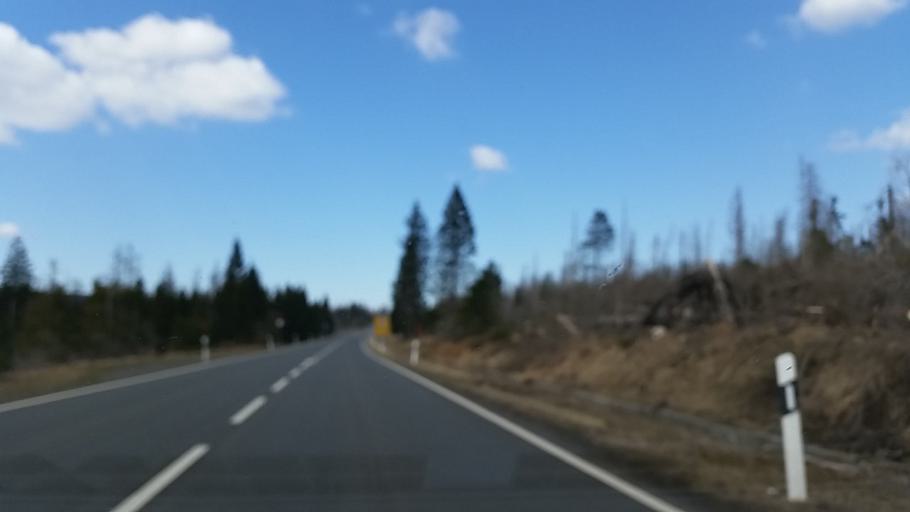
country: DE
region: Lower Saxony
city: Sankt Andreasberg
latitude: 51.7584
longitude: 10.5511
